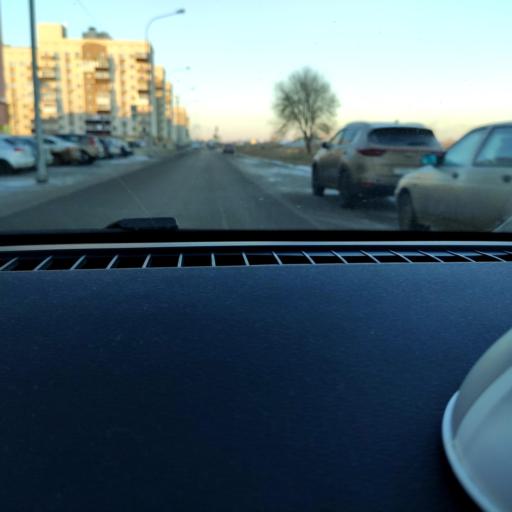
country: RU
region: Samara
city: Samara
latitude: 53.1162
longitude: 50.1498
